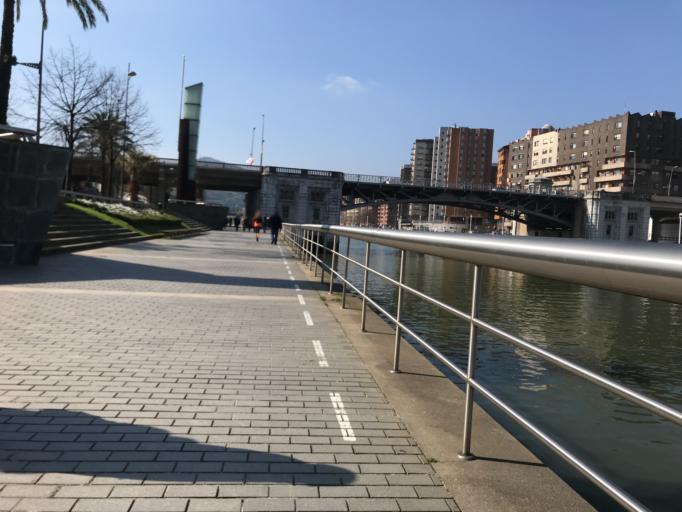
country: ES
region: Basque Country
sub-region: Bizkaia
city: Bilbao
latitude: 43.2694
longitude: -2.9392
